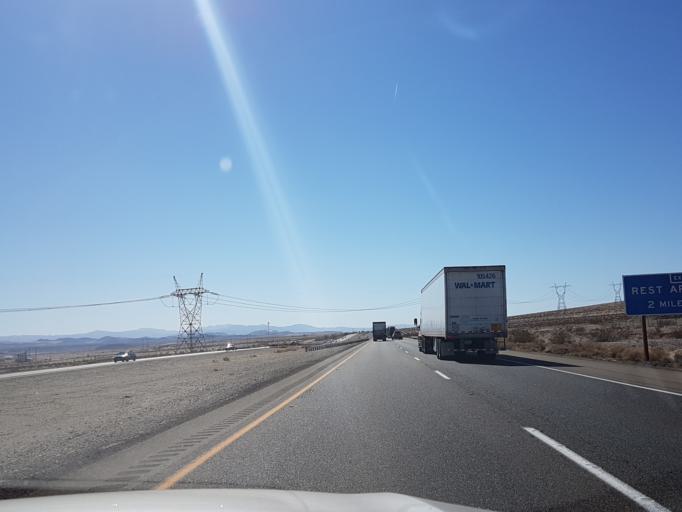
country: US
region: California
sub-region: San Bernardino County
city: Fort Irwin
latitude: 35.0530
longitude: -116.4401
